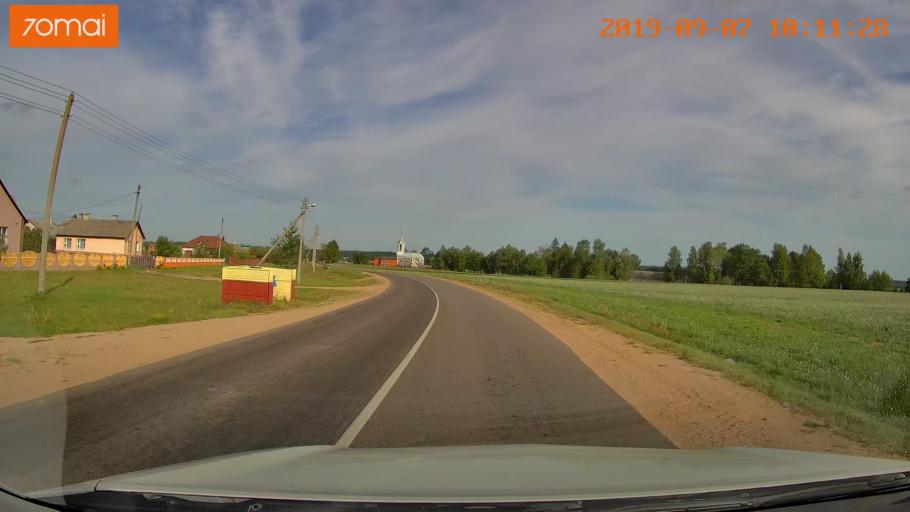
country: BY
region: Grodnenskaya
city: Voranava
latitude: 54.1234
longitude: 25.3660
